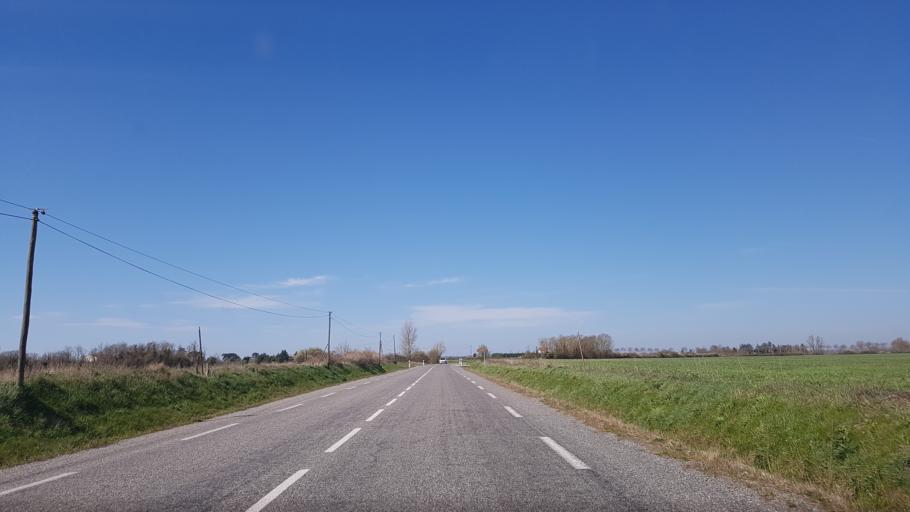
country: FR
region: Midi-Pyrenees
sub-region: Departement de l'Ariege
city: Mazeres
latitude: 43.2298
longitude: 1.6694
